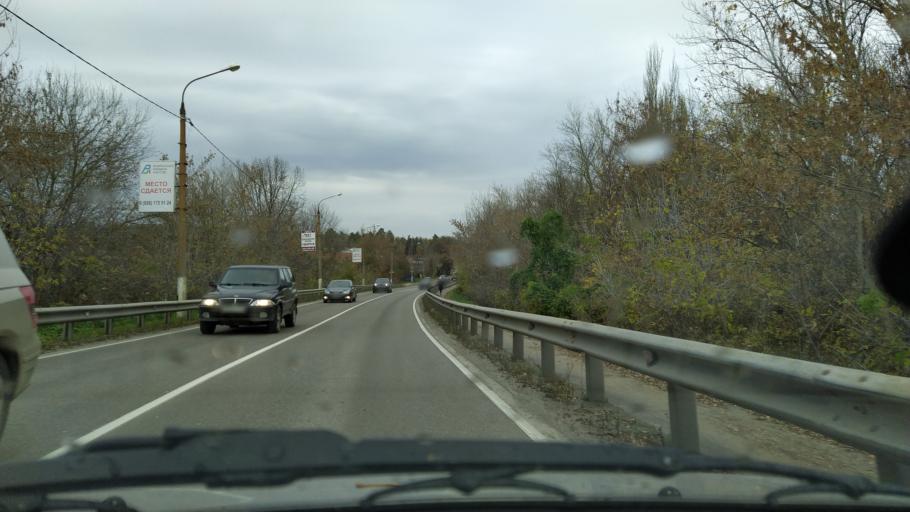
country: RU
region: Moskovskaya
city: Voskresensk
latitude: 55.3232
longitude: 38.6534
